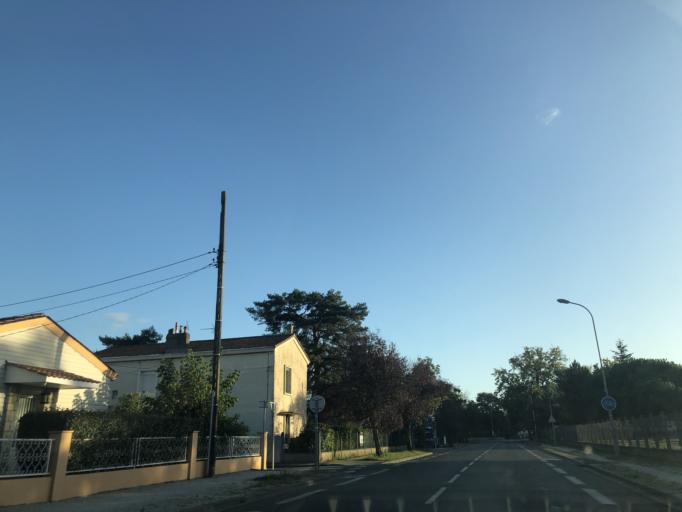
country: FR
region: Aquitaine
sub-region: Departement de la Gironde
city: Merignac
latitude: 44.8440
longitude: -0.6361
